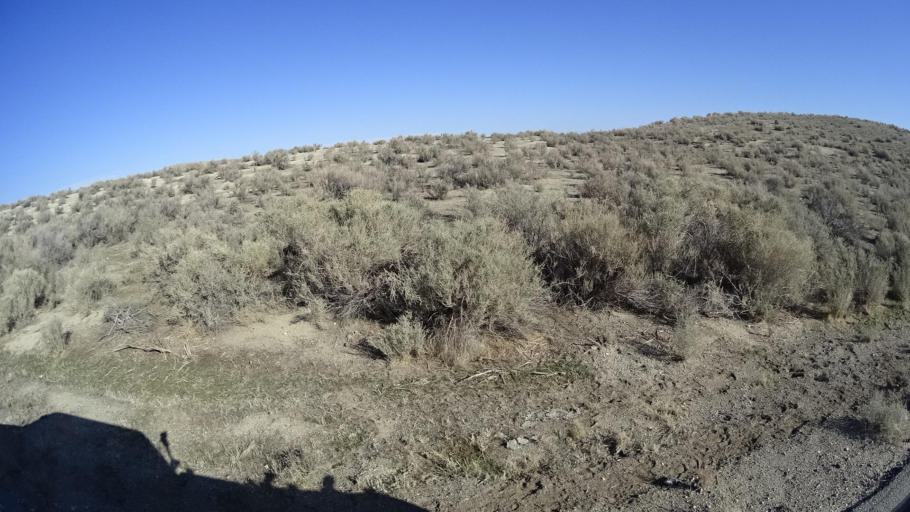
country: US
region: California
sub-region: Kern County
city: Taft Heights
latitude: 35.2305
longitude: -119.6455
